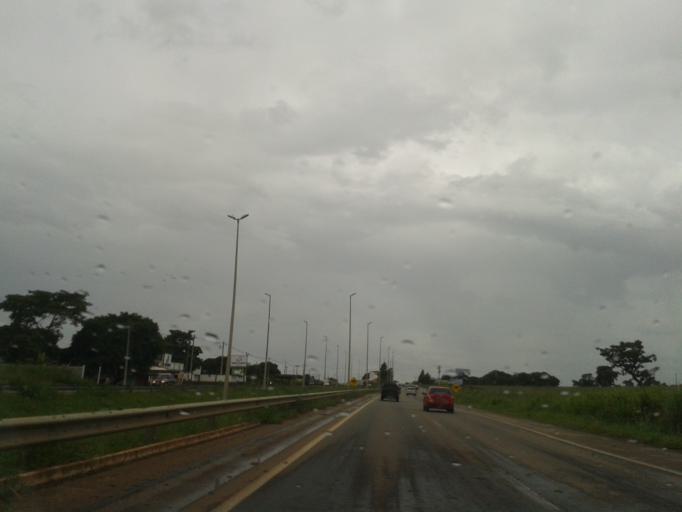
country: BR
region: Goias
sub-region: Goiania
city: Goiania
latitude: -16.6159
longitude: -49.3606
